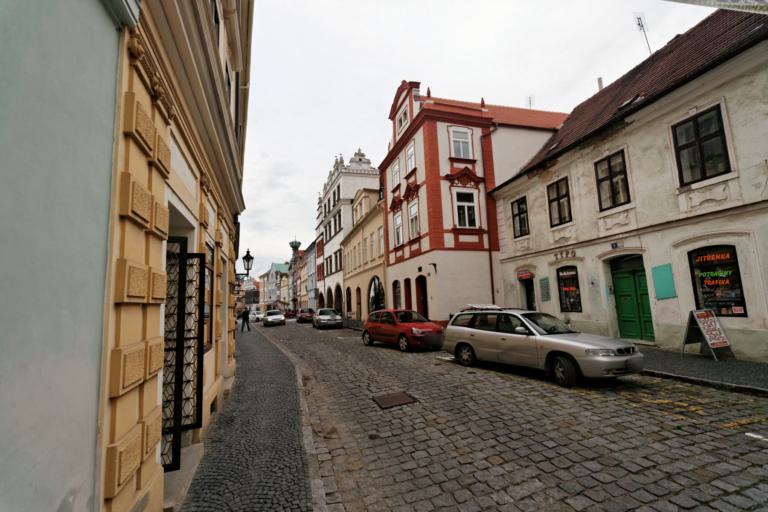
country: CZ
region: Ustecky
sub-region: Okres Litomerice
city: Litomerice
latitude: 50.5343
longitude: 14.1296
